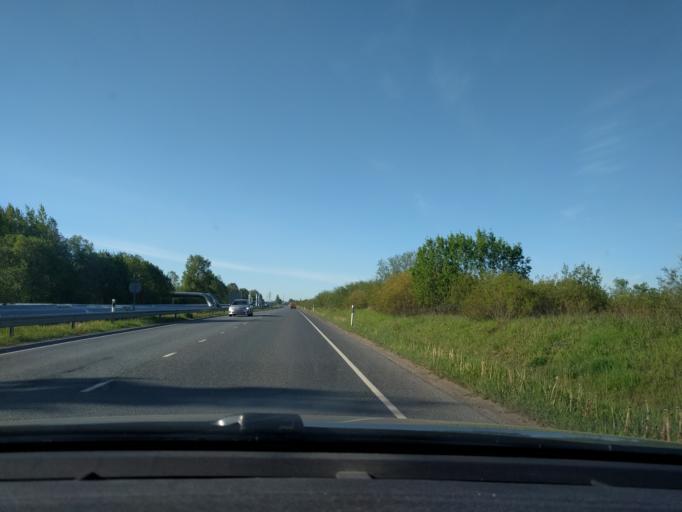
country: EE
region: Harju
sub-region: Maardu linn
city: Maardu
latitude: 59.4783
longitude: 24.9814
